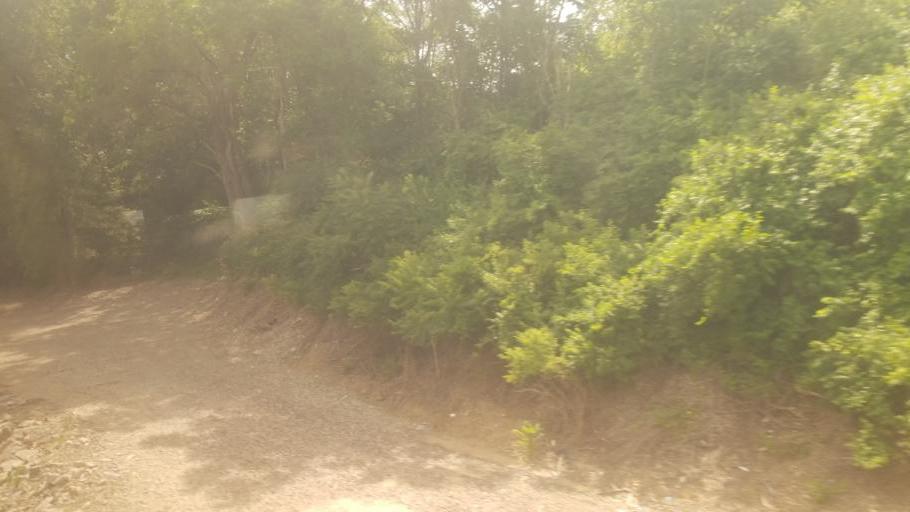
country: US
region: Missouri
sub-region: Jackson County
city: Sugar Creek
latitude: 39.1128
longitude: -94.4879
